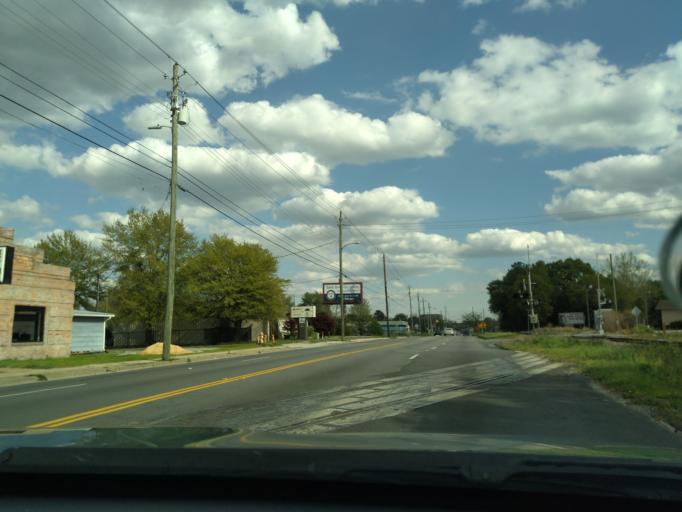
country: US
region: South Carolina
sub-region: Florence County
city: Florence
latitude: 34.2086
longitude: -79.7734
